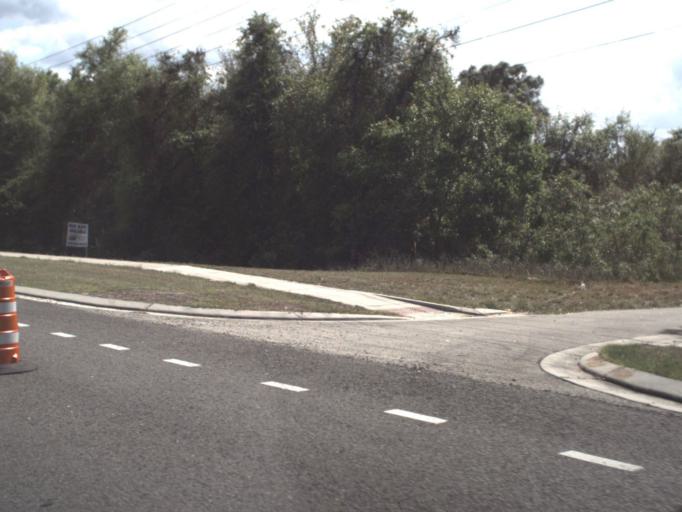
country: US
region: Florida
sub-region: Lake County
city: Clermont
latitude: 28.4941
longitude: -81.7167
